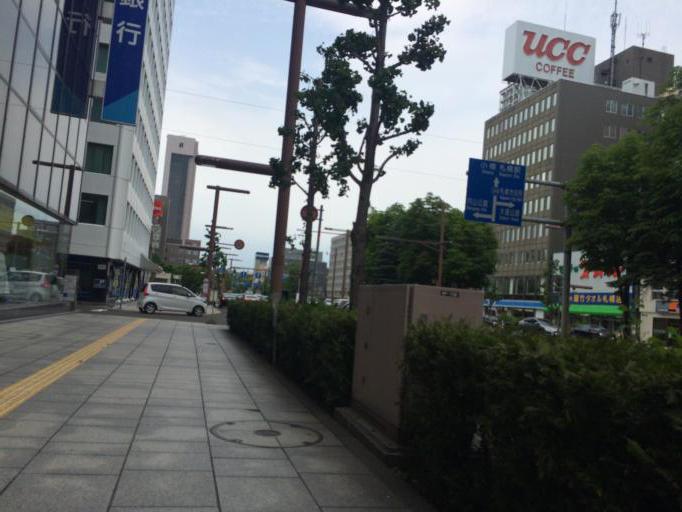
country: JP
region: Hokkaido
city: Sapporo
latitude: 43.0577
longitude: 141.3412
